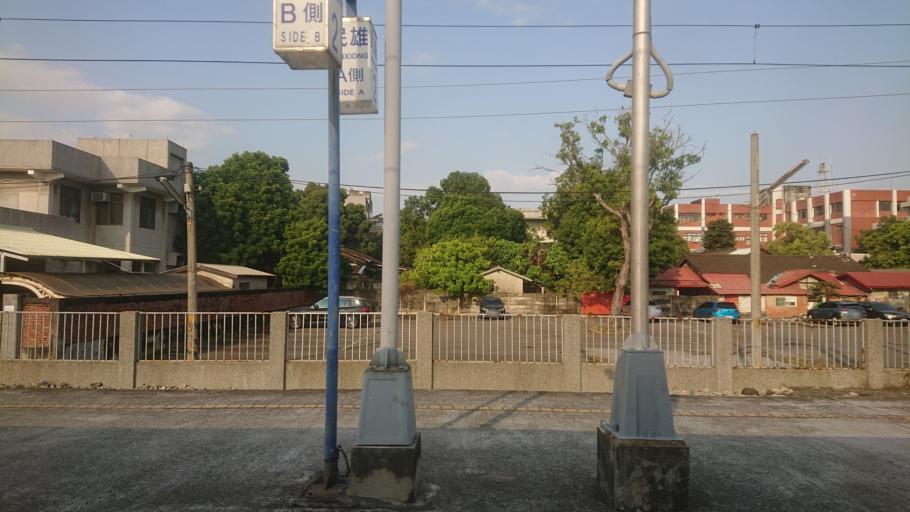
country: TW
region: Taiwan
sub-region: Chiayi
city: Jiayi Shi
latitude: 23.5542
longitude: 120.4311
